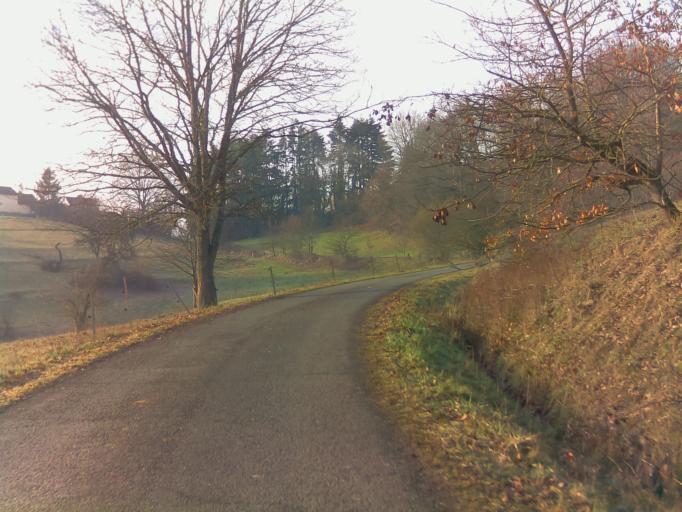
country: DE
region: Rheinland-Pfalz
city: Gries
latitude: 49.4205
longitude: 7.4092
